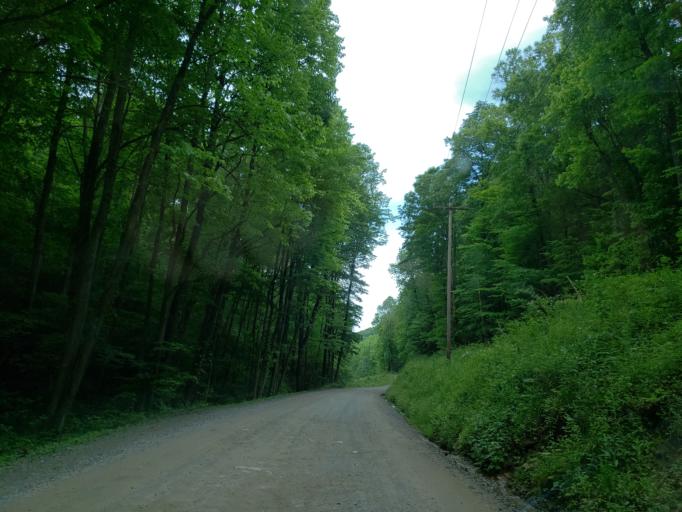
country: US
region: Georgia
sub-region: Fannin County
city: Blue Ridge
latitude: 34.8457
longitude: -84.4166
